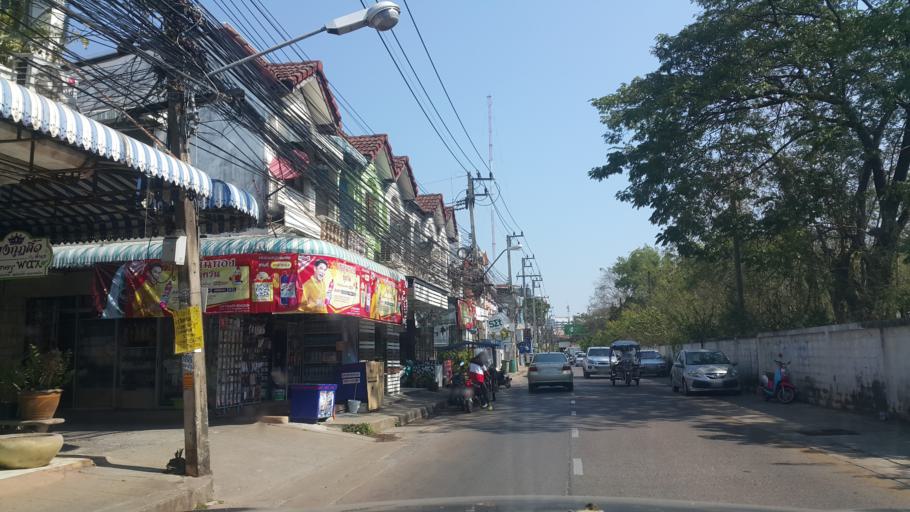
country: TH
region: Changwat Udon Thani
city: Udon Thani
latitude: 17.3941
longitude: 102.7955
